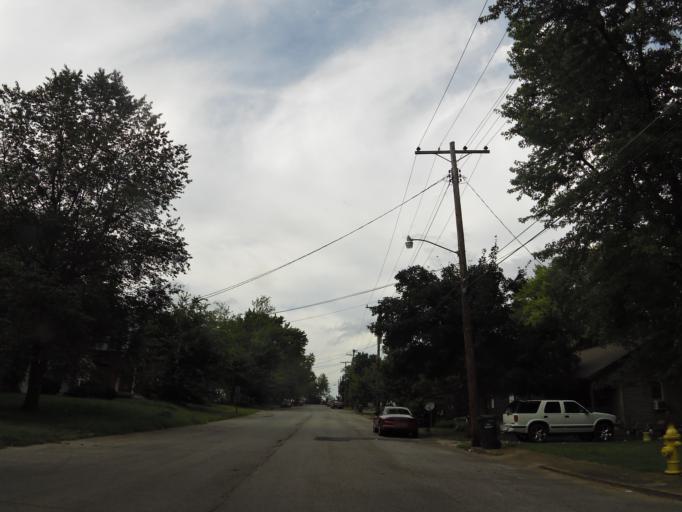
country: US
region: Kentucky
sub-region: Christian County
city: Hopkinsville
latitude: 36.8728
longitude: -87.4919
